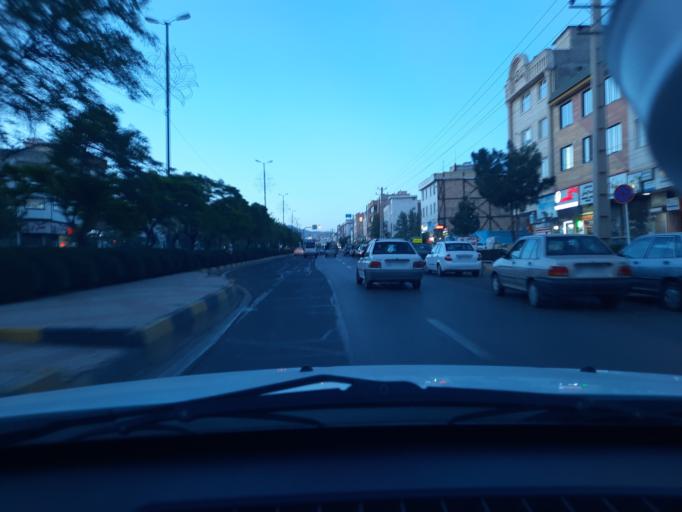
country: IR
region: Qazvin
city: Qazvin
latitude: 36.3095
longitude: 50.0132
